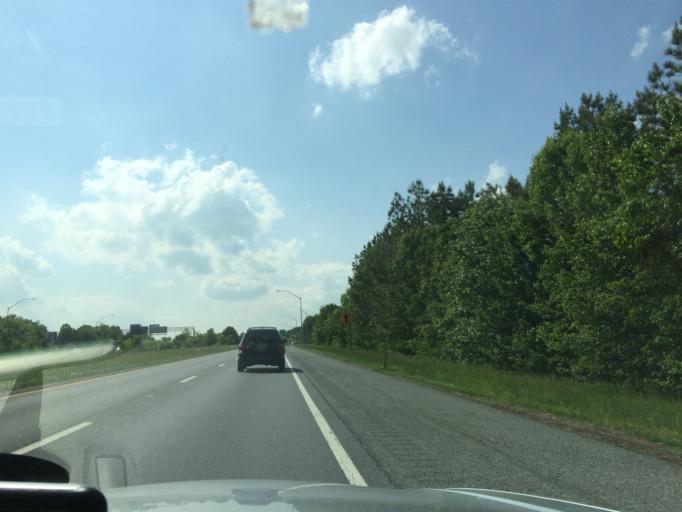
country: US
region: Maryland
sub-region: Howard County
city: Riverside
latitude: 39.1806
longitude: -76.8711
